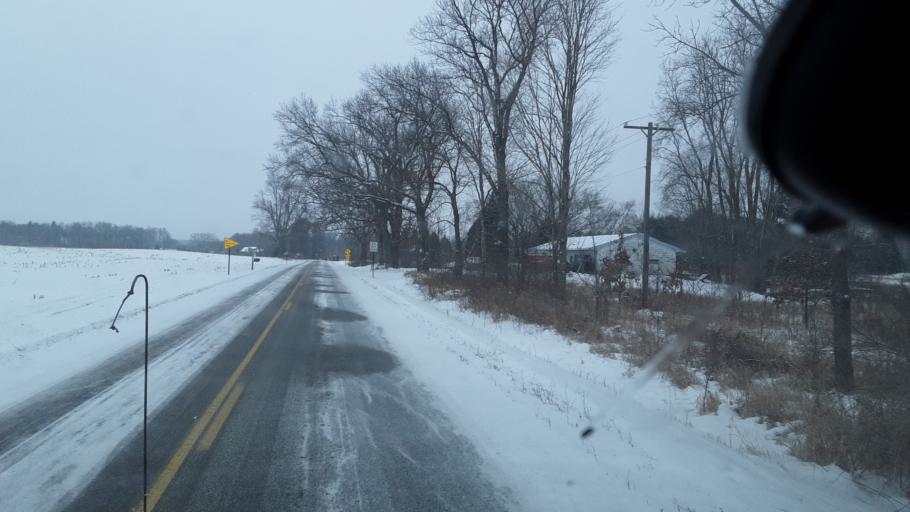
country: US
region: Michigan
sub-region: Ingham County
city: Leslie
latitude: 42.4276
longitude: -84.3168
